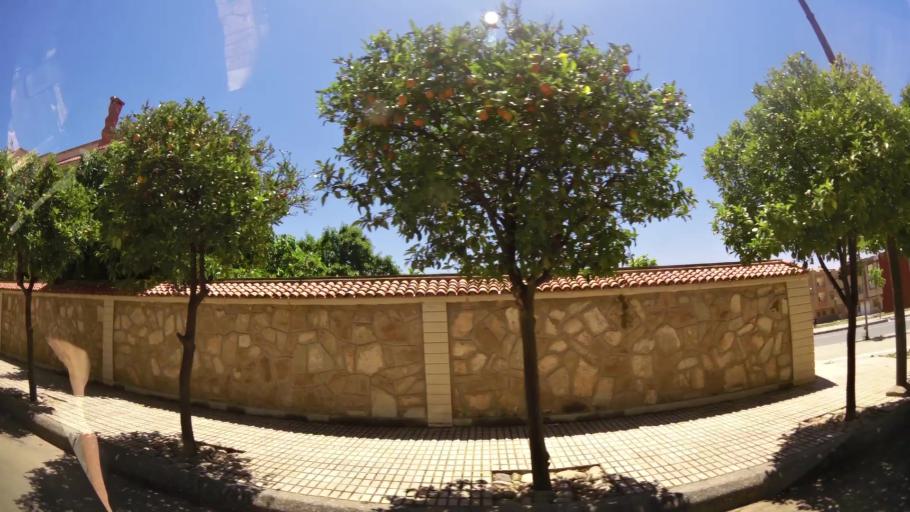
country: MA
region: Oriental
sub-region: Oujda-Angad
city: Oujda
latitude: 34.6681
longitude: -1.8728
